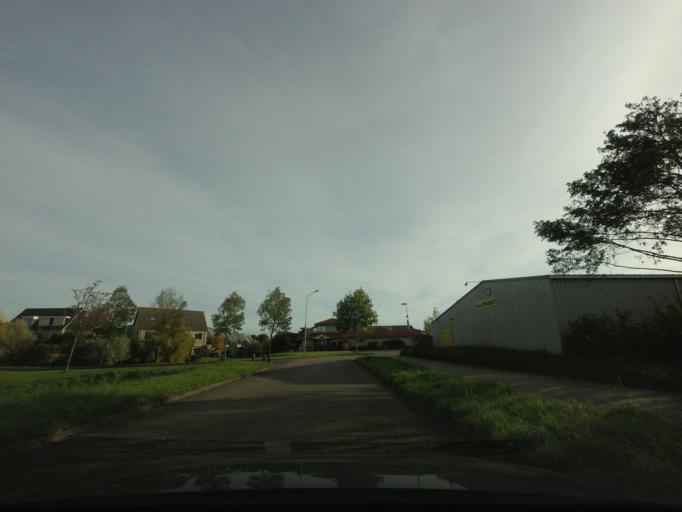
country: NL
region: North Holland
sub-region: Gemeente Langedijk
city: Broek op Langedijk
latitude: 52.7077
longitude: 4.8038
